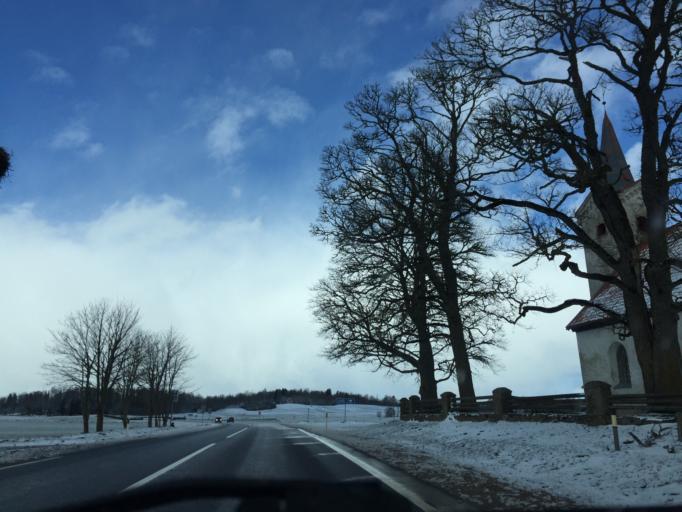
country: LV
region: Kandava
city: Kandava
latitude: 57.1374
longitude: 22.7344
